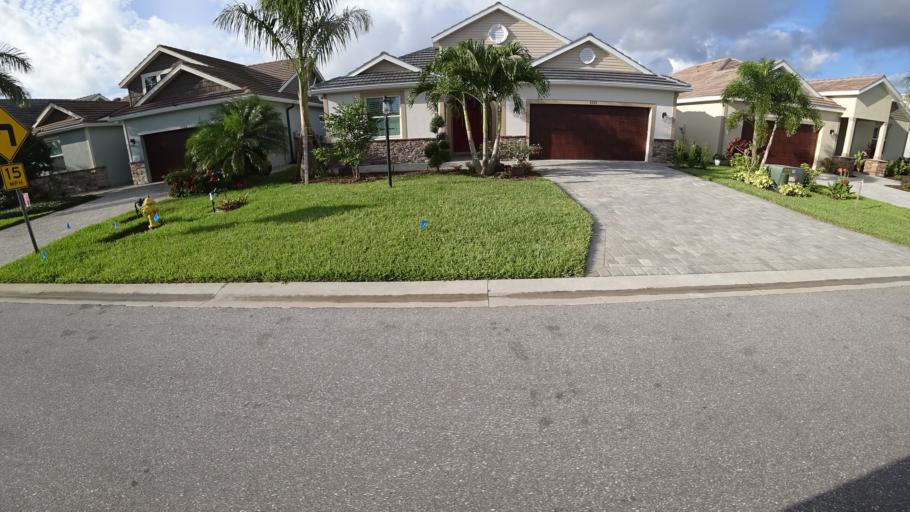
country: US
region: Florida
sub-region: Sarasota County
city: Desoto Lakes
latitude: 27.4245
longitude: -82.4882
